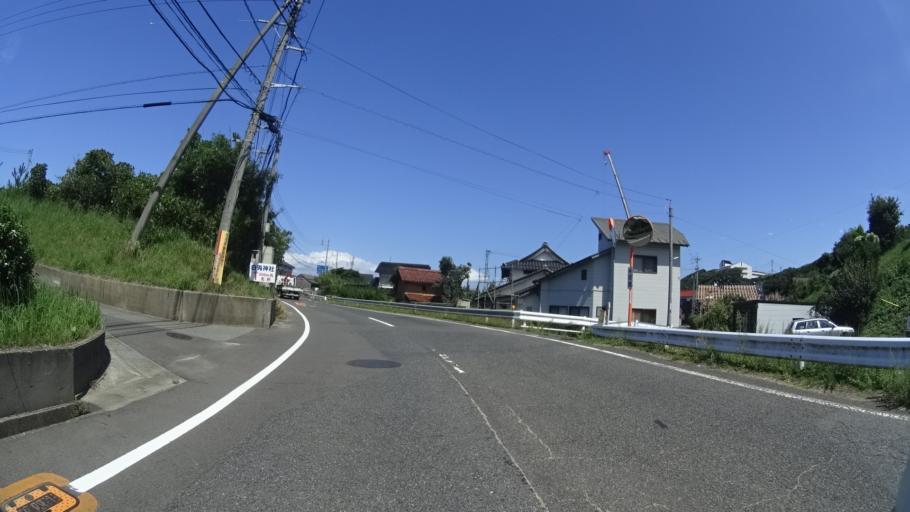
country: JP
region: Tottori
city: Tottori
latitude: 35.5233
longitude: 134.1167
